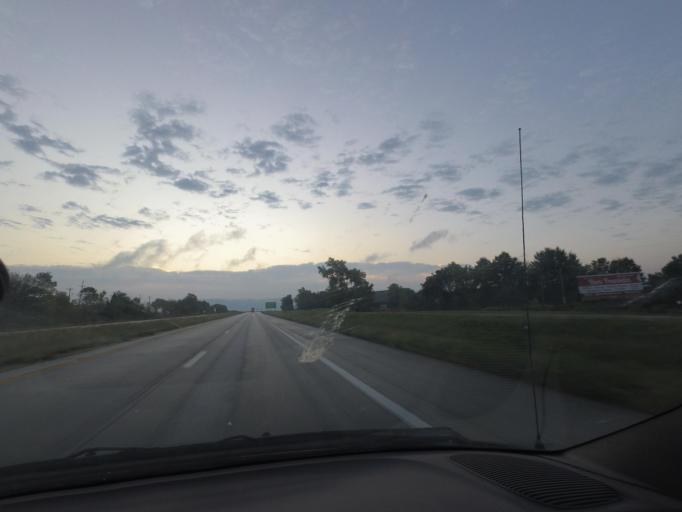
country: US
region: Missouri
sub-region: Macon County
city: Macon
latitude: 39.7488
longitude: -92.5139
